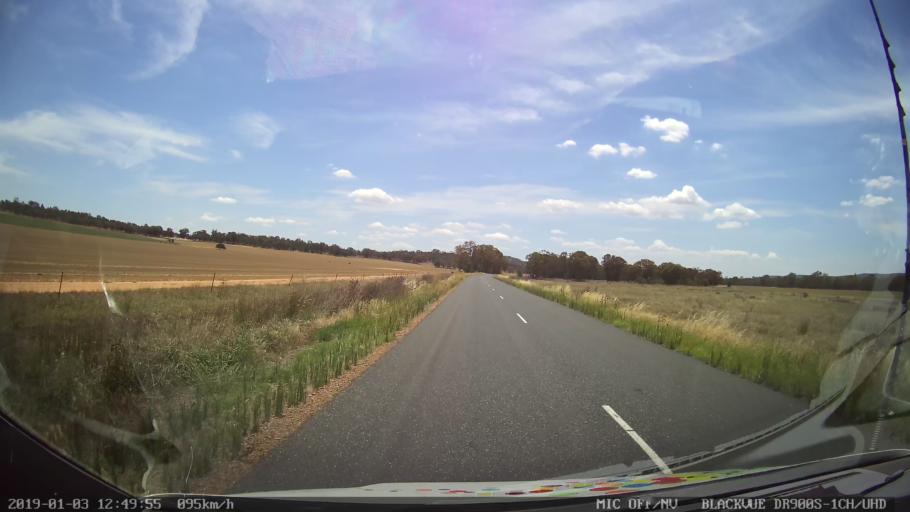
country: AU
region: New South Wales
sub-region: Weddin
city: Grenfell
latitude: -33.6973
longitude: 148.2650
